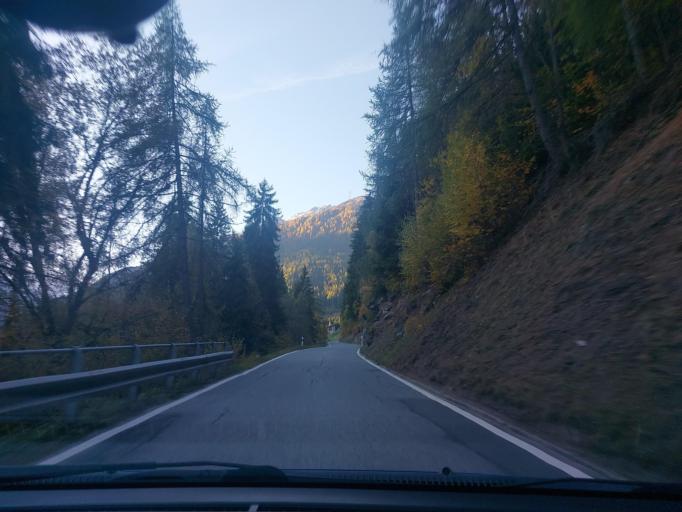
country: CH
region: Valais
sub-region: Sierre District
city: Chippis
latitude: 46.1897
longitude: 7.5844
